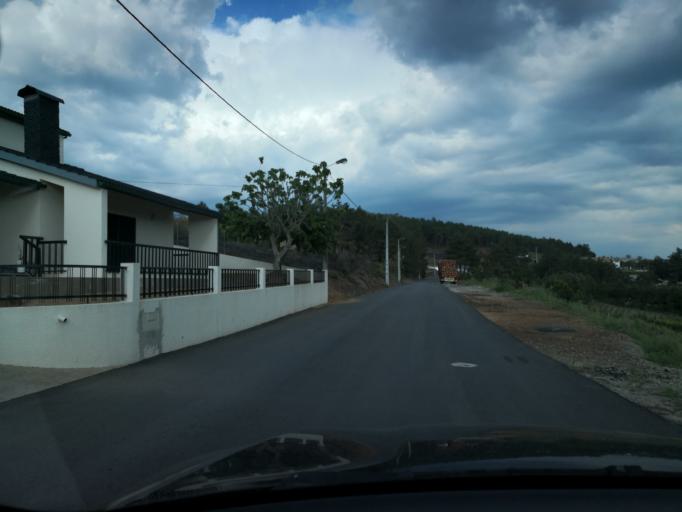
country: PT
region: Vila Real
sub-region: Sabrosa
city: Vilela
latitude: 41.2214
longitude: -7.6785
